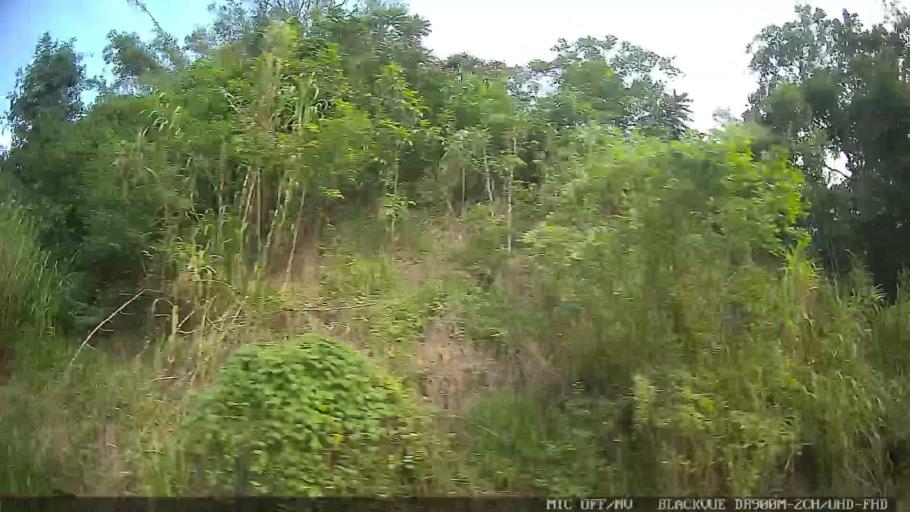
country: BR
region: Sao Paulo
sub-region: Serra Negra
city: Serra Negra
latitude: -22.7026
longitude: -46.6565
